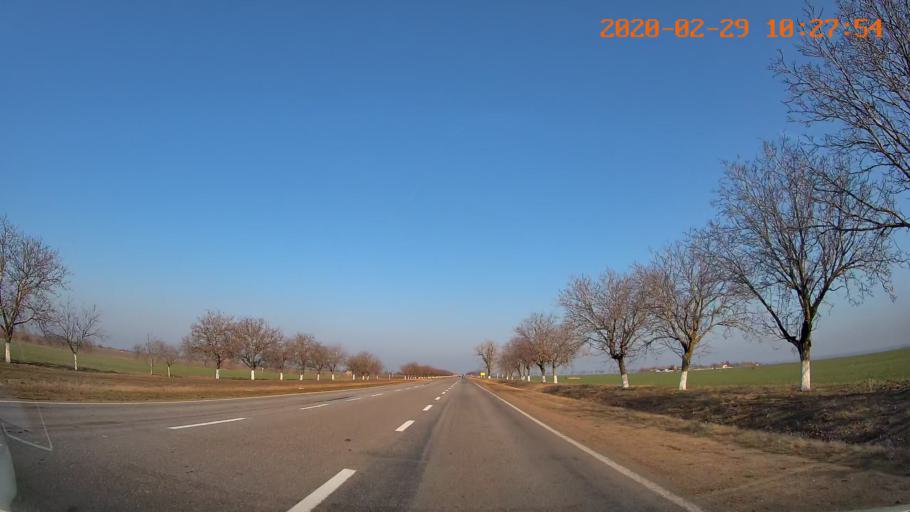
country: MD
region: Telenesti
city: Tiraspolul Nou
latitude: 46.9026
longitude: 29.5950
